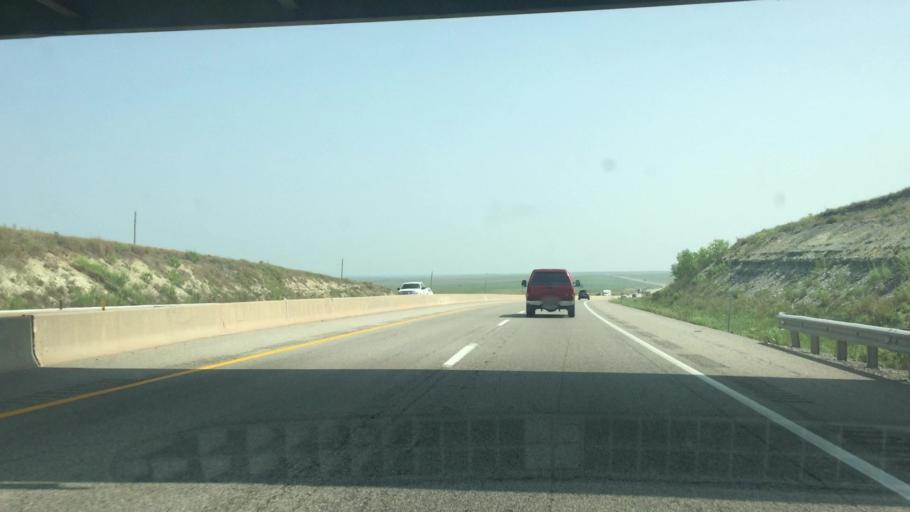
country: US
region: Kansas
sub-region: Chase County
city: Cottonwood Falls
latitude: 38.2758
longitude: -96.3732
